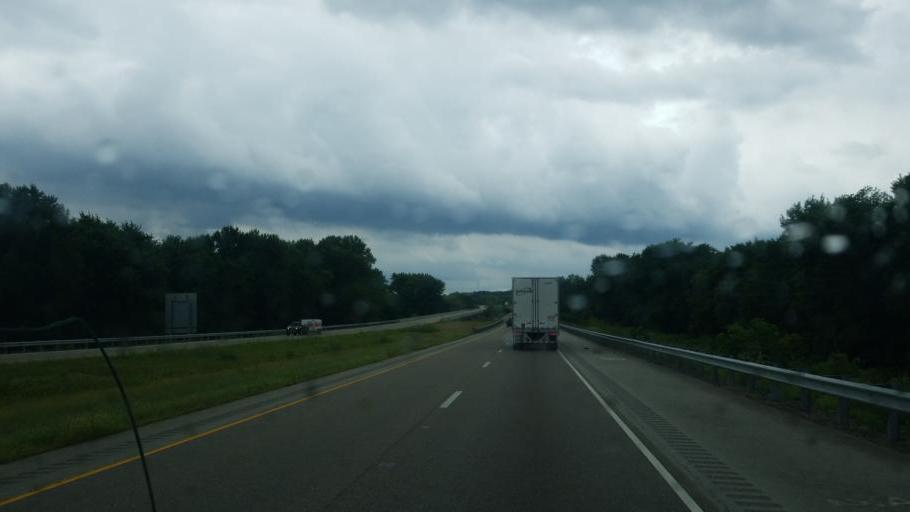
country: US
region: Illinois
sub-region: Cumberland County
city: Greenup
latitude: 39.2545
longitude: -88.1666
